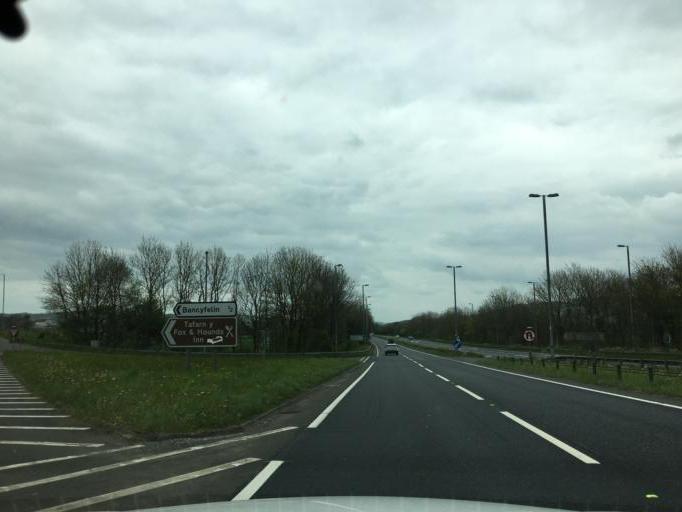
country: GB
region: Wales
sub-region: Carmarthenshire
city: Llangynog
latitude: 51.8301
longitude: -4.4419
